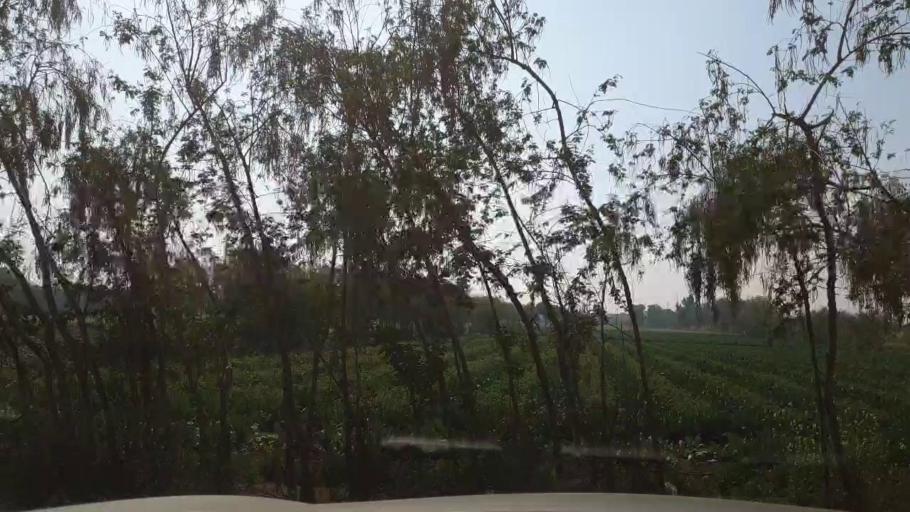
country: PK
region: Sindh
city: Tando Allahyar
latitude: 25.6082
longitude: 68.6946
